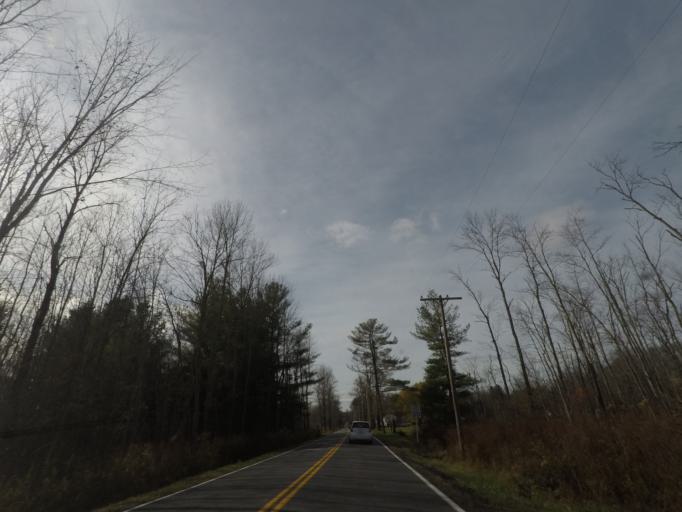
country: US
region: New York
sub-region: Schenectady County
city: Rotterdam
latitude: 42.7549
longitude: -73.9769
